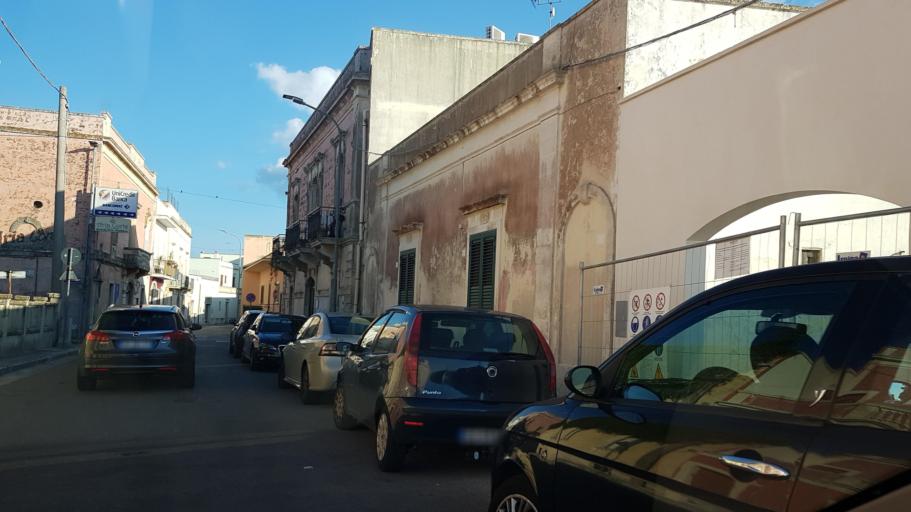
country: IT
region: Apulia
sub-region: Provincia di Lecce
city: Marittima
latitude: 39.9973
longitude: 18.3970
